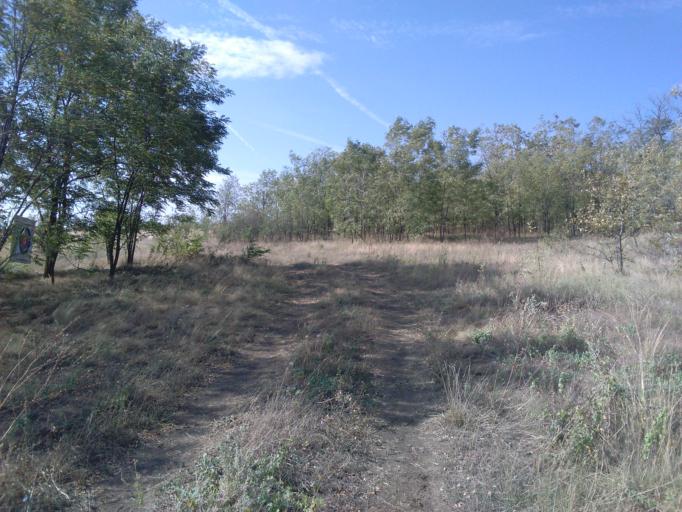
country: RU
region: Rostov
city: Gornyy
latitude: 47.8884
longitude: 40.2408
